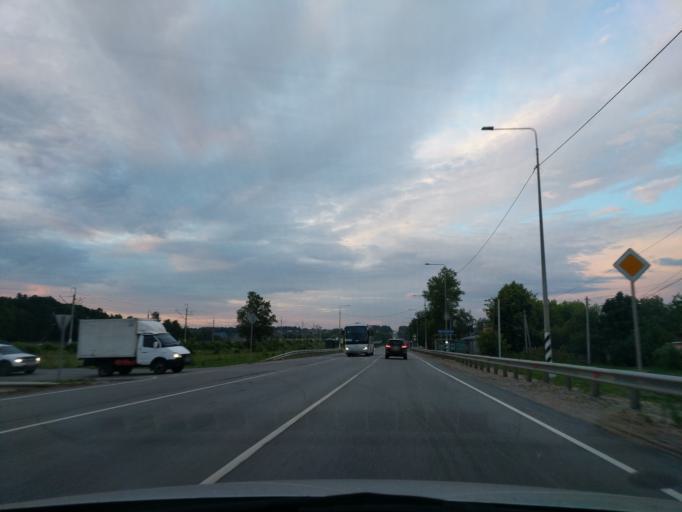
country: RU
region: Kaluga
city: Obninsk
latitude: 55.0542
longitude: 36.5714
